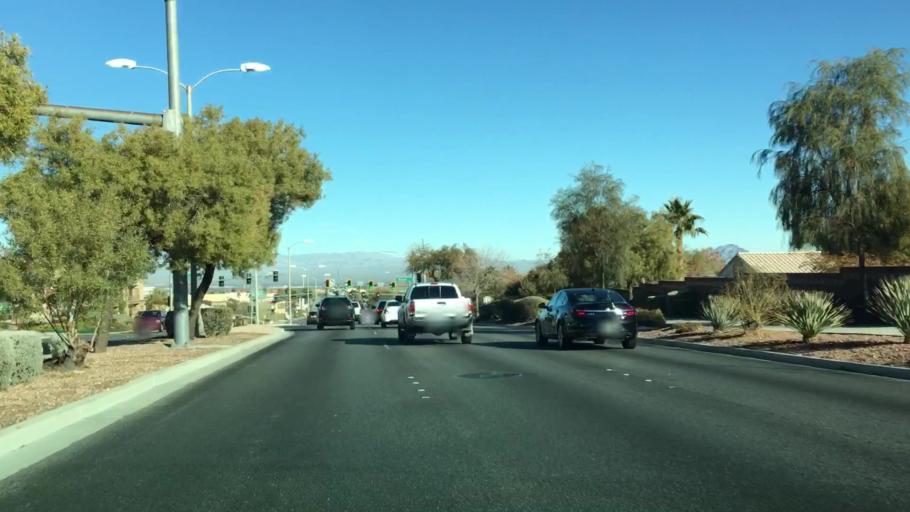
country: US
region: Nevada
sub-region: Clark County
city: Whitney
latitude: 35.9869
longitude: -115.1009
